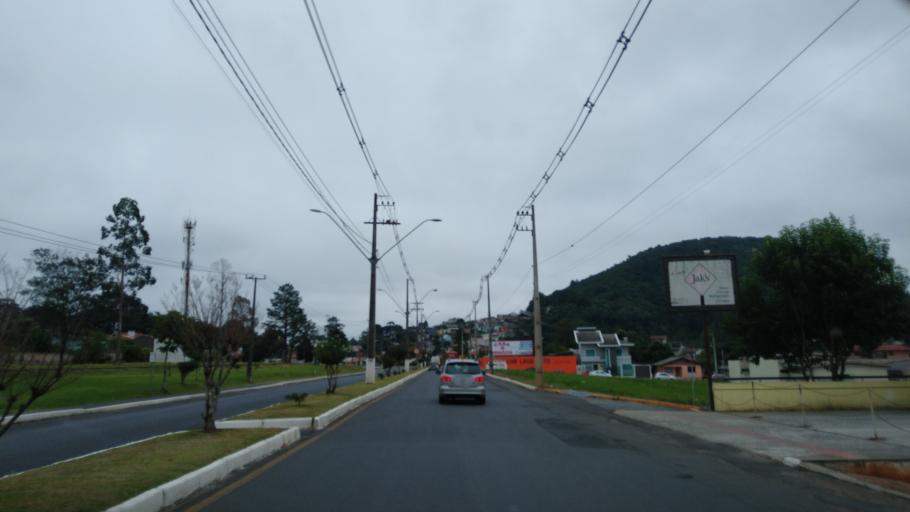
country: BR
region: Santa Catarina
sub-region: Porto Uniao
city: Porto Uniao
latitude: -26.2574
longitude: -51.0734
